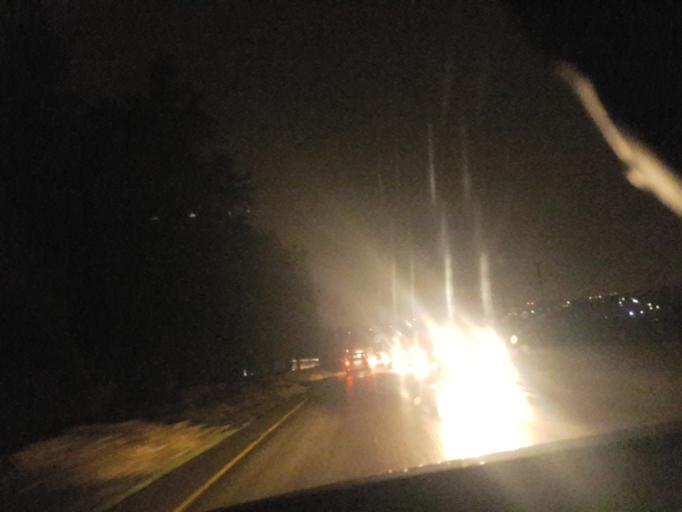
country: ZA
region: Gauteng
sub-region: City of Johannesburg Metropolitan Municipality
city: Diepsloot
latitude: -25.9756
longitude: 27.9497
